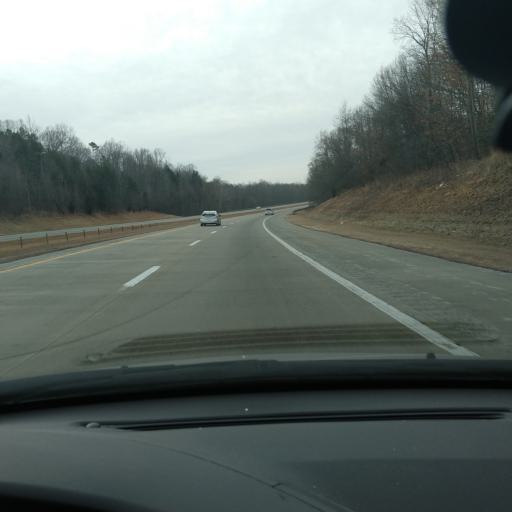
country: US
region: North Carolina
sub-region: Davidson County
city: Welcome
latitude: 35.8841
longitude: -80.2306
